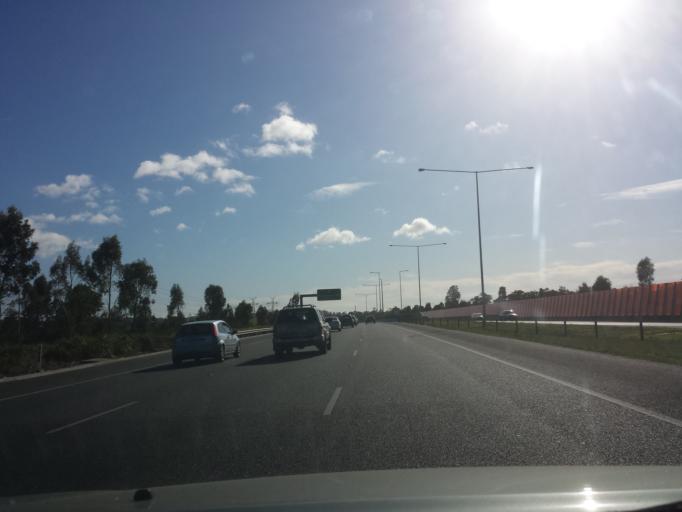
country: AU
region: Victoria
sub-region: Knox
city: Wantirna
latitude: -37.8481
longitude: 145.2165
